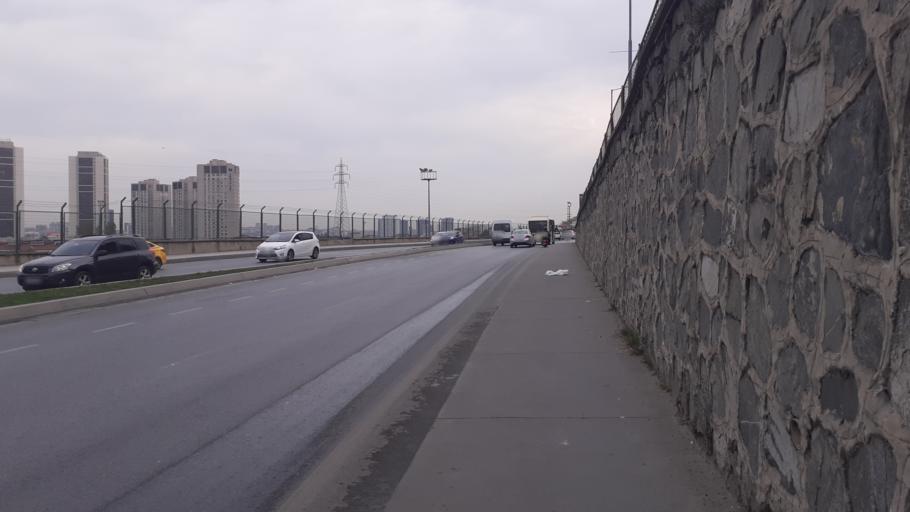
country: TR
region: Istanbul
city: Basaksehir
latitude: 41.0615
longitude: 28.7888
